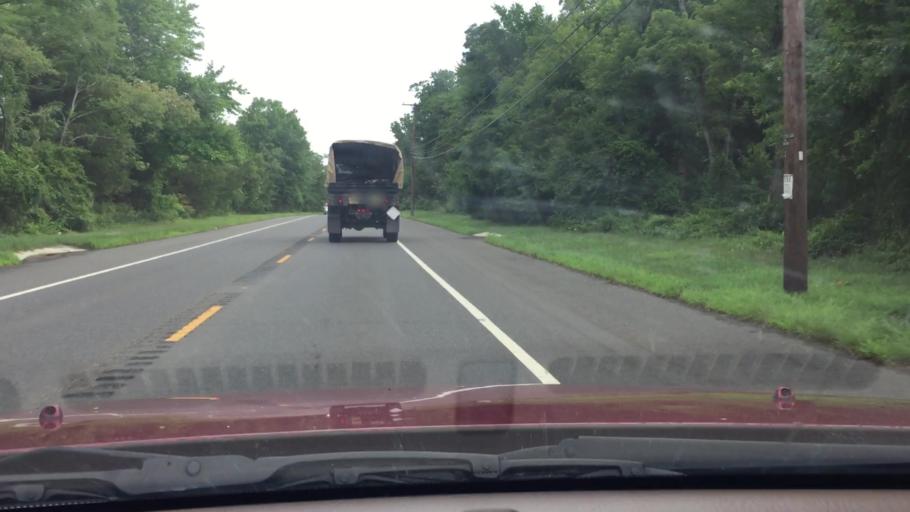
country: US
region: New Jersey
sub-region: Burlington County
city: Fort Dix
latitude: 40.0463
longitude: -74.6465
